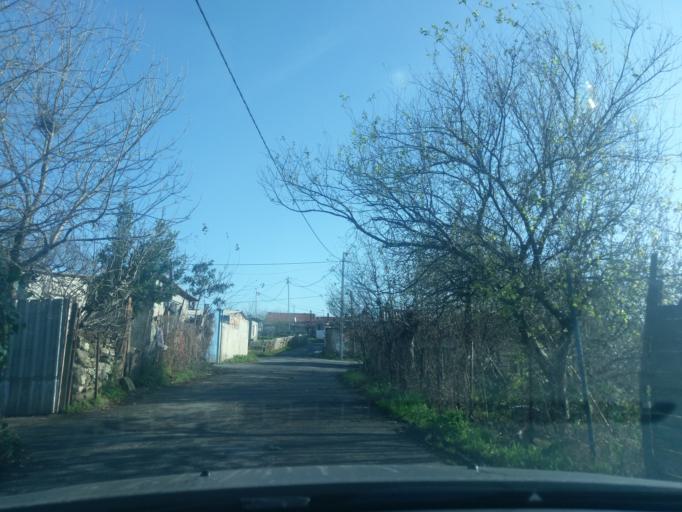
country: TR
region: Istanbul
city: Sultangazi
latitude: 41.1333
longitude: 28.8430
